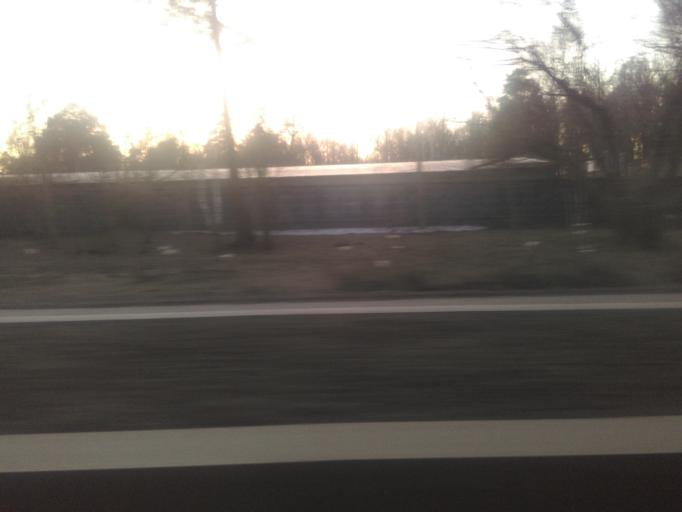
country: RU
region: Moskovskaya
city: Bol'shaya Setun'
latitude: 55.7072
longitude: 37.4210
